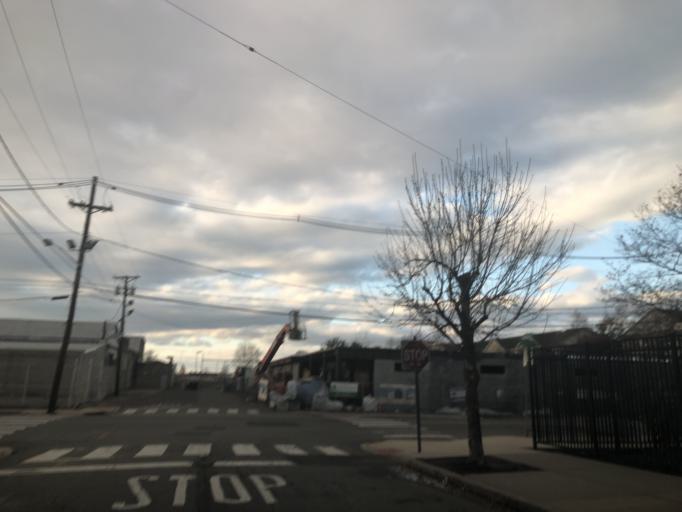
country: US
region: New Jersey
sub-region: Hudson County
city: Jersey City
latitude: 40.7150
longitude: -74.0918
